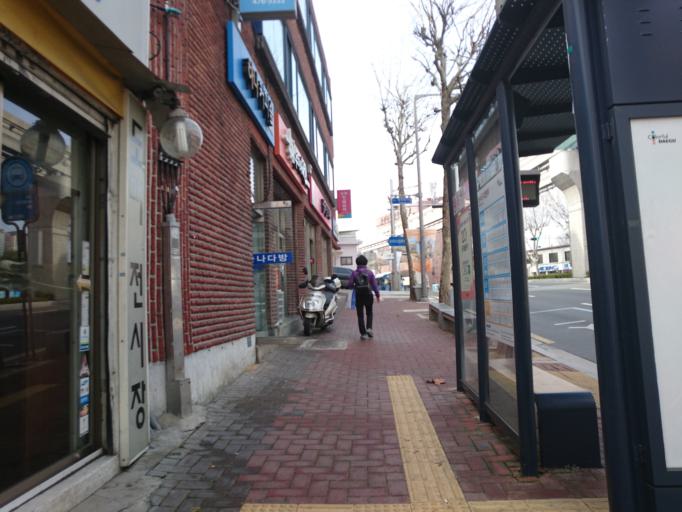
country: KR
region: Daegu
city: Daegu
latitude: 35.8559
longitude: 128.5975
